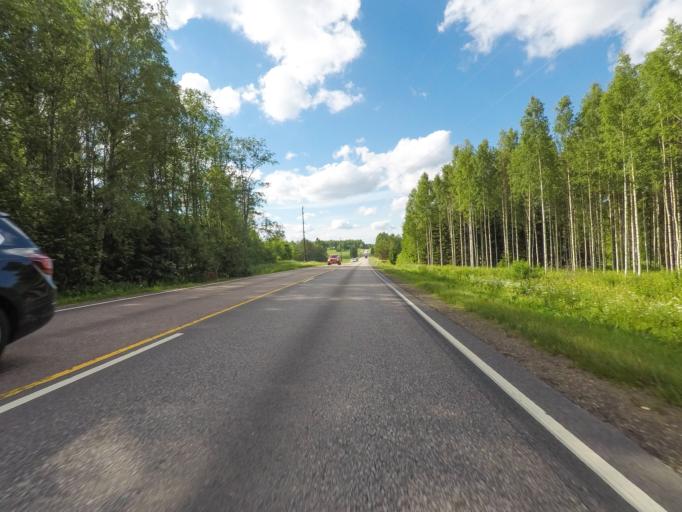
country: FI
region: Southern Savonia
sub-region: Savonlinna
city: Kerimaeki
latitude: 61.8639
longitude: 29.1424
